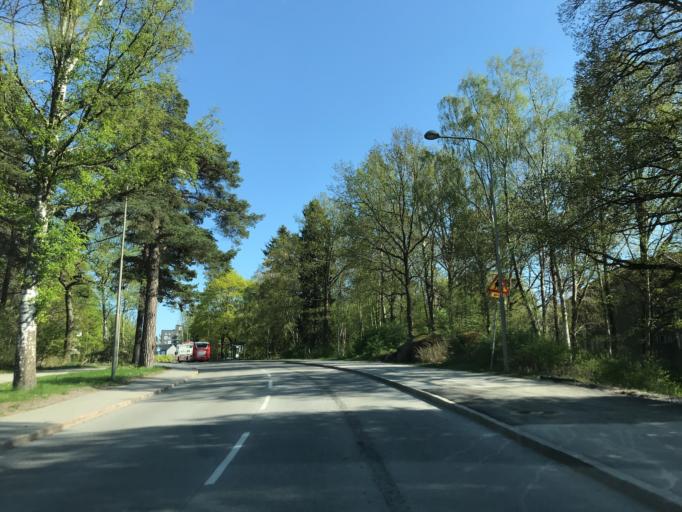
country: SE
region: Stockholm
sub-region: Stockholms Kommun
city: Arsta
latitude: 59.2902
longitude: 18.0000
